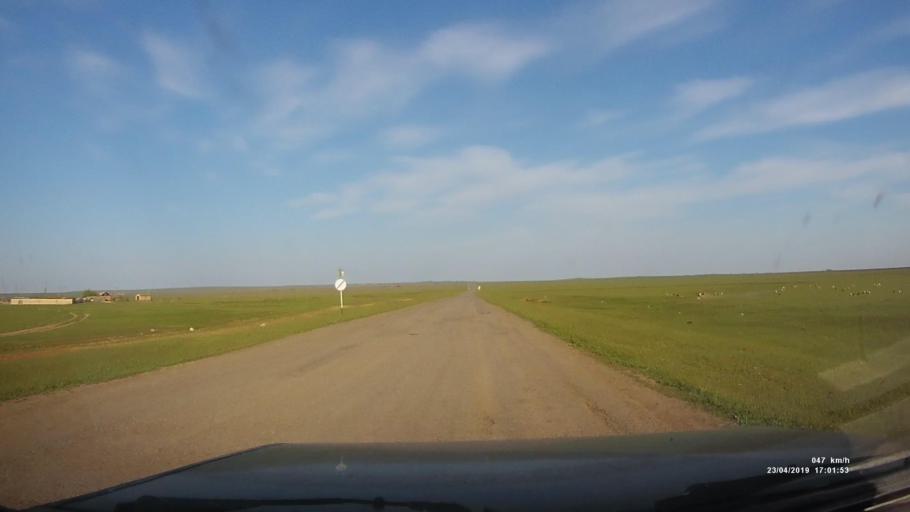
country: RU
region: Kalmykiya
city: Priyutnoye
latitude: 46.2942
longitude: 43.4107
